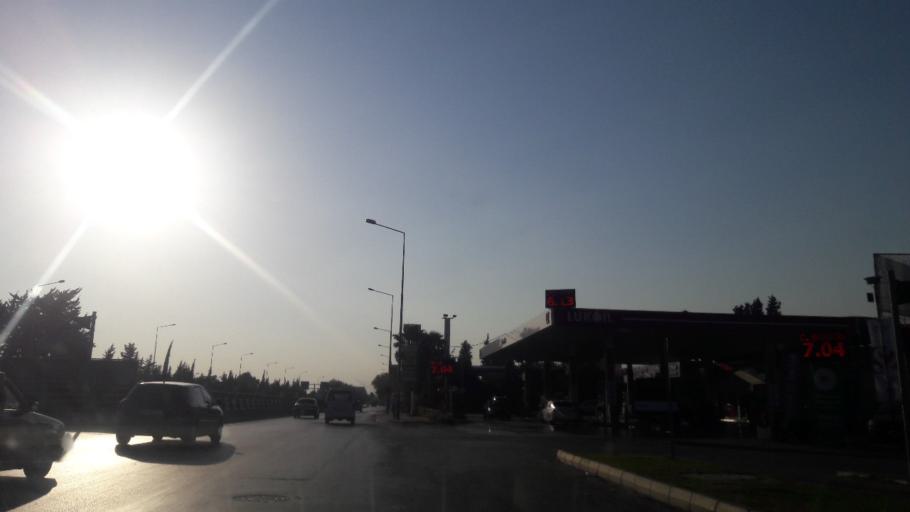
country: TR
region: Adana
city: Seyhan
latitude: 36.9936
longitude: 35.2997
